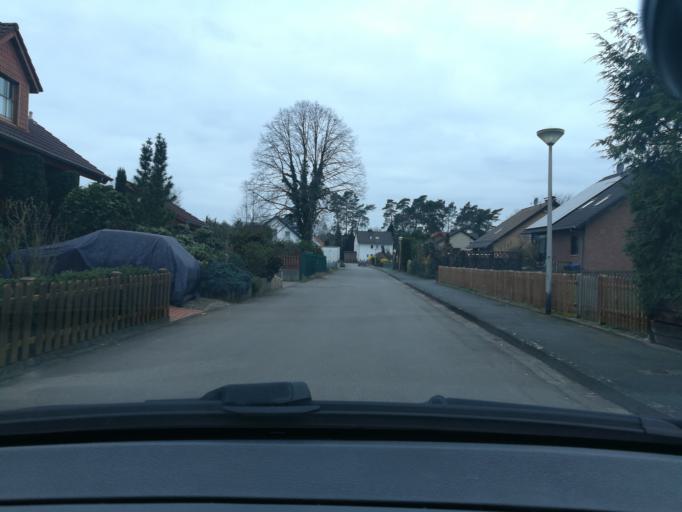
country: DE
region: North Rhine-Westphalia
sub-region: Regierungsbezirk Detmold
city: Oerlinghausen
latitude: 51.9341
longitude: 8.6299
